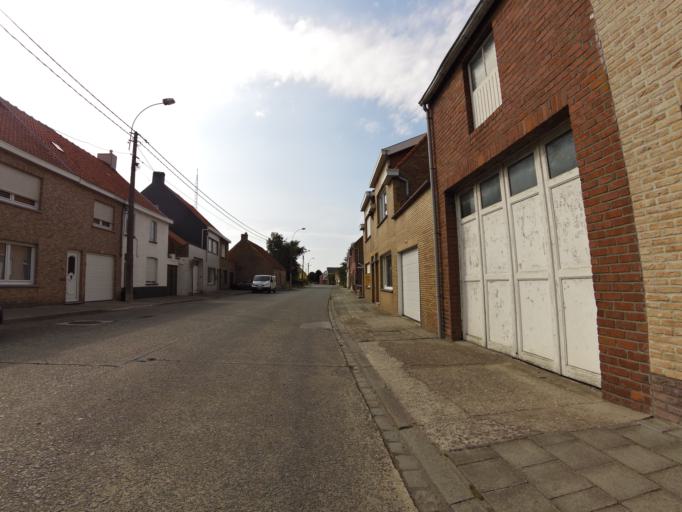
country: BE
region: Flanders
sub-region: Provincie West-Vlaanderen
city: Oudenburg
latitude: 51.1818
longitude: 3.0235
